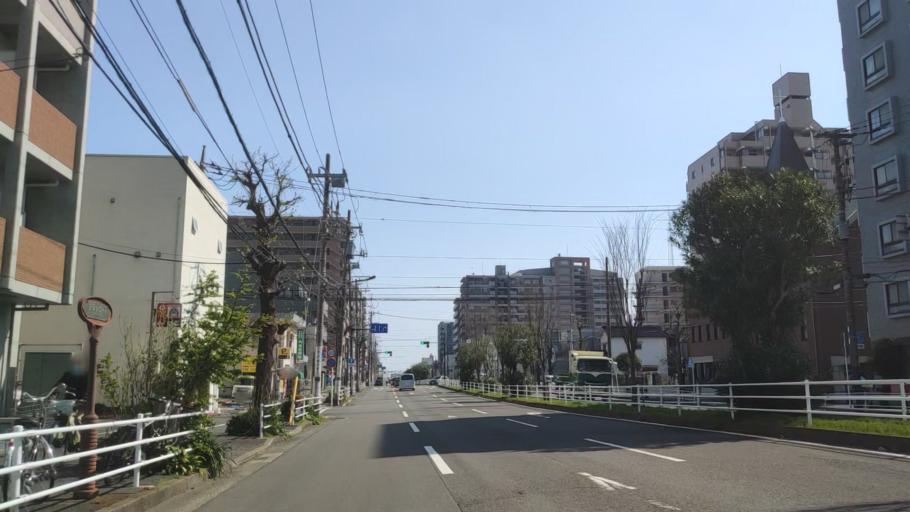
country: JP
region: Kanagawa
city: Hiratsuka
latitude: 35.3321
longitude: 139.3447
